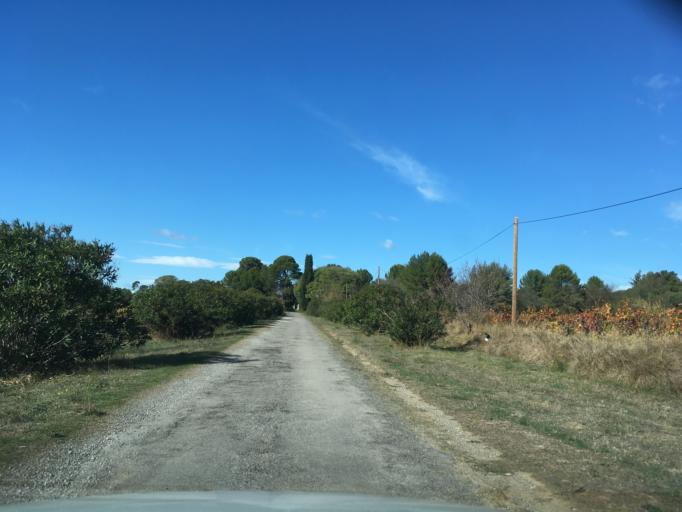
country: FR
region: Languedoc-Roussillon
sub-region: Departement de l'Herault
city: Saint-Jean-de-Vedas
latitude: 43.5849
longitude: 3.8490
